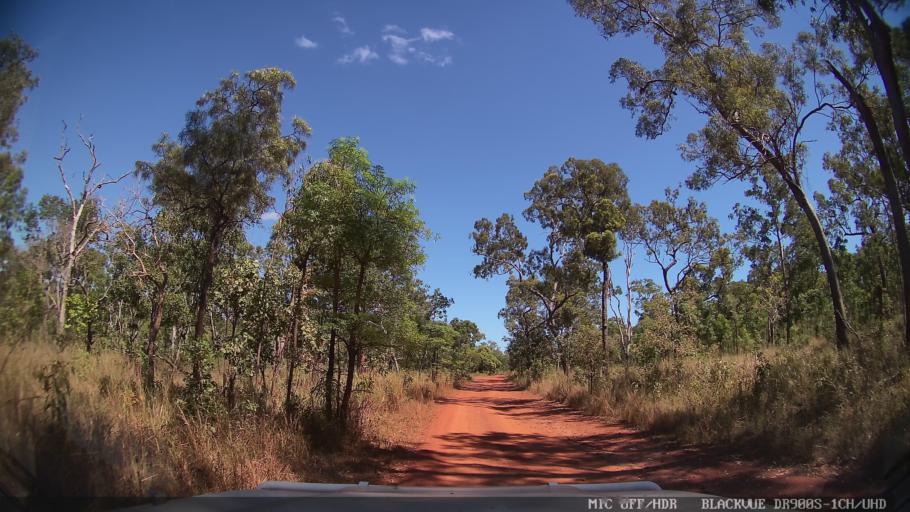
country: AU
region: Queensland
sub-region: Torres
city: Thursday Island
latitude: -10.9134
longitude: 142.2493
